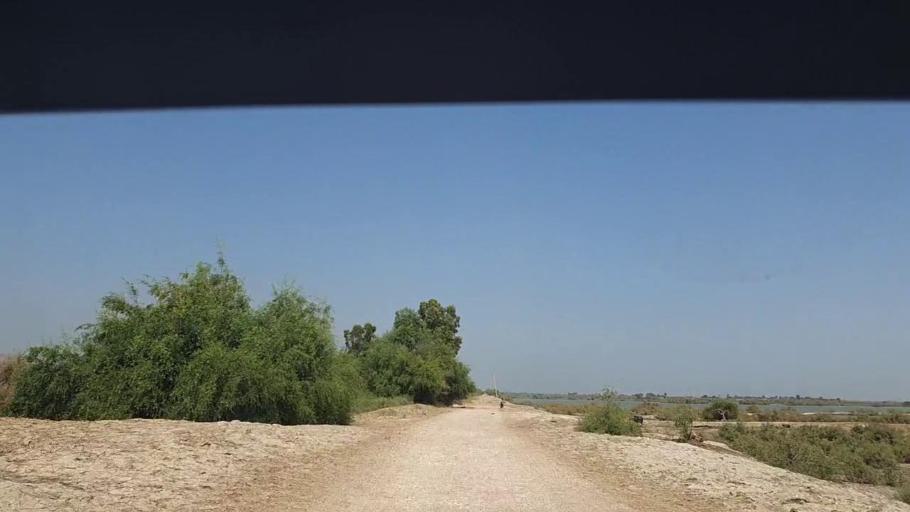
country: PK
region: Sindh
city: Kandhkot
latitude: 28.1939
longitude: 69.1683
